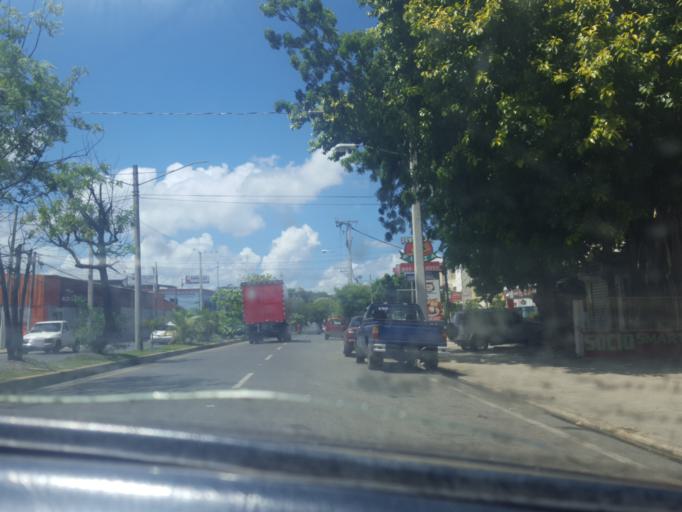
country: DO
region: Santiago
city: Santiago de los Caballeros
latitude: 19.4903
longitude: -70.7033
